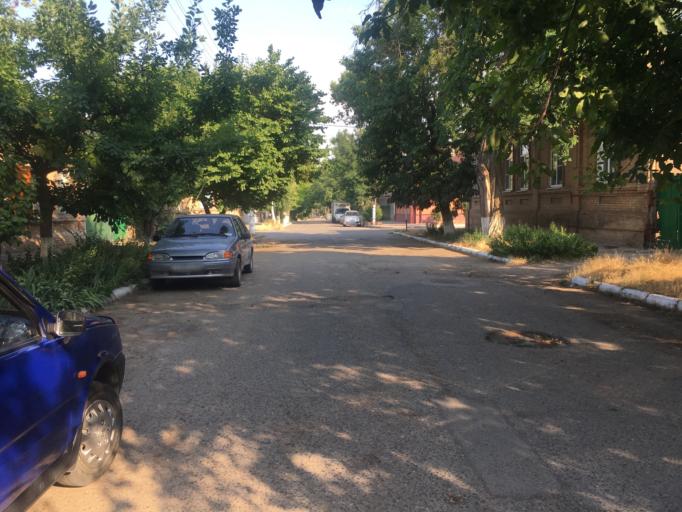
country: RU
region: Krasnodarskiy
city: Yeysk
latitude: 46.7156
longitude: 38.2726
